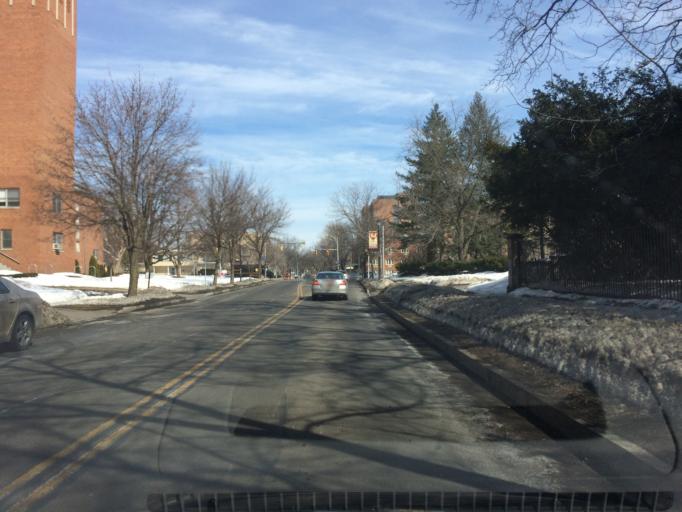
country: US
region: New York
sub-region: Monroe County
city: Rochester
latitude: 43.1524
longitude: -77.5887
